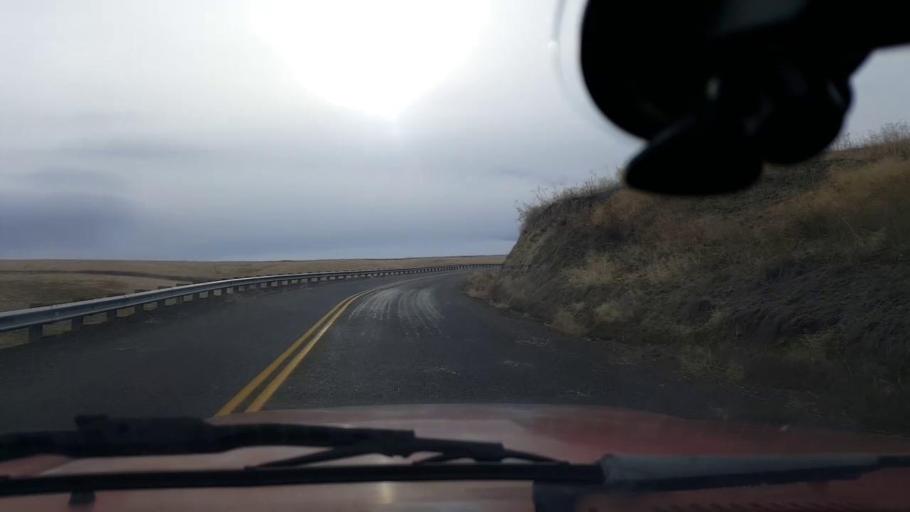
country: US
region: Washington
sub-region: Asotin County
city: Clarkston Heights-Vineland
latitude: 46.3819
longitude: -117.1390
